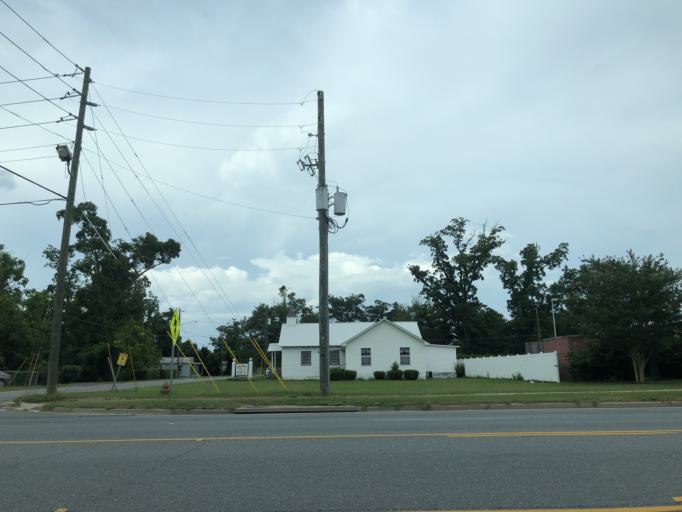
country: US
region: Georgia
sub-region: Wayne County
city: Jesup
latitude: 31.6100
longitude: -81.8840
